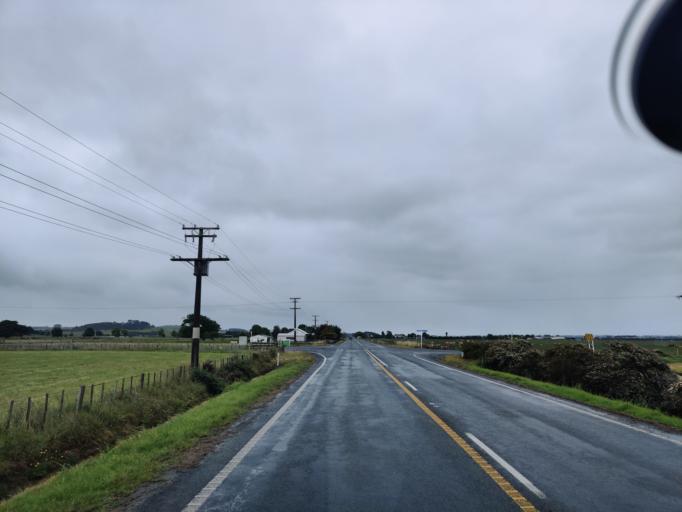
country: NZ
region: Northland
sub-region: Kaipara District
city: Dargaville
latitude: -35.9513
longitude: 173.8922
